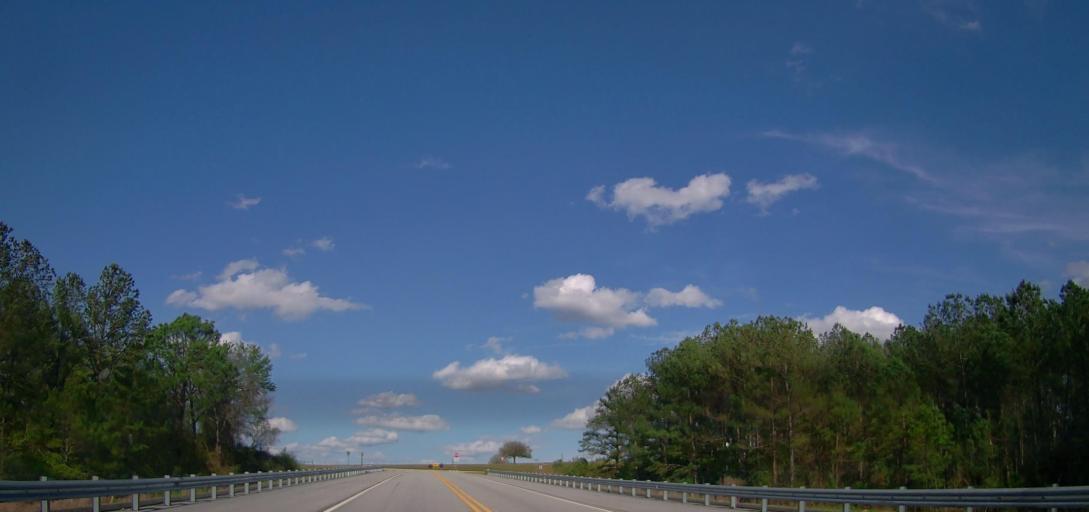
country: US
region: Georgia
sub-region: Baldwin County
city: Hardwick
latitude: 33.0179
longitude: -83.1023
